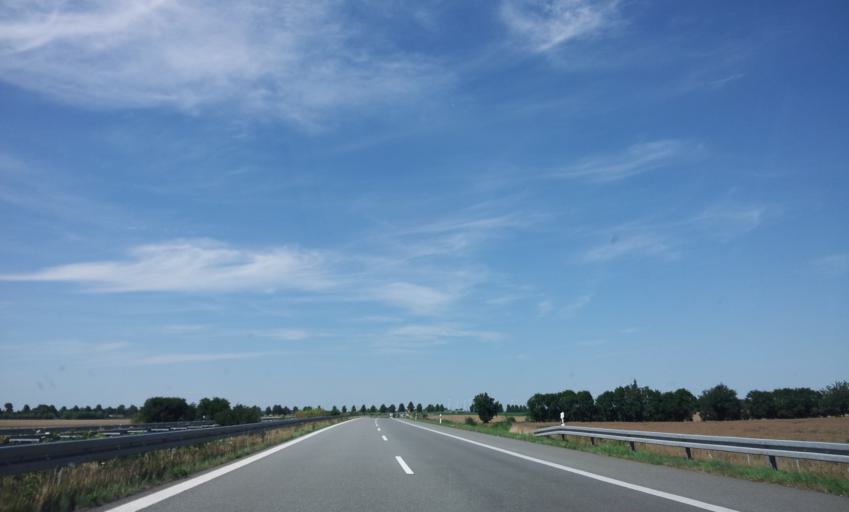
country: DE
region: Mecklenburg-Vorpommern
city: Gormin
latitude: 54.0061
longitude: 13.3000
